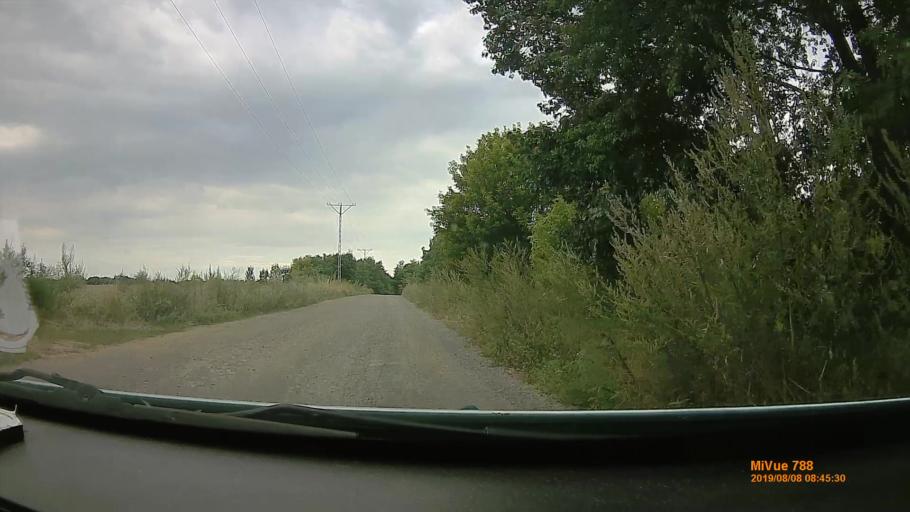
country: HU
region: Hajdu-Bihar
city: Debrecen
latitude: 47.5949
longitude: 21.6381
